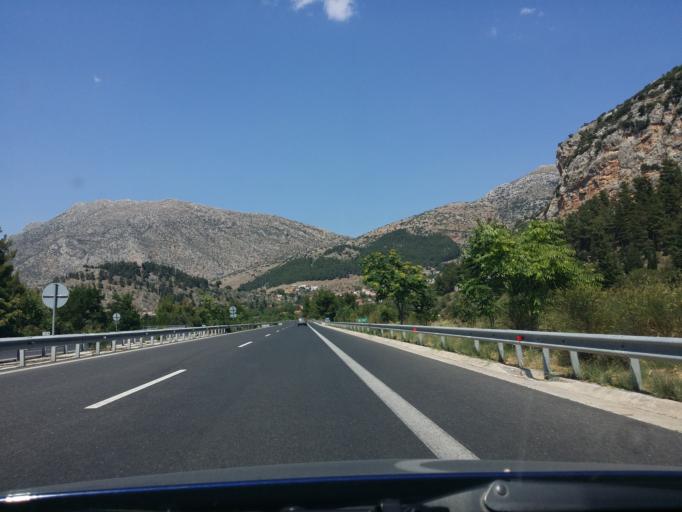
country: GR
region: Peloponnese
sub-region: Nomos Arkadias
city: Tripoli
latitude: 37.6074
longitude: 22.4537
